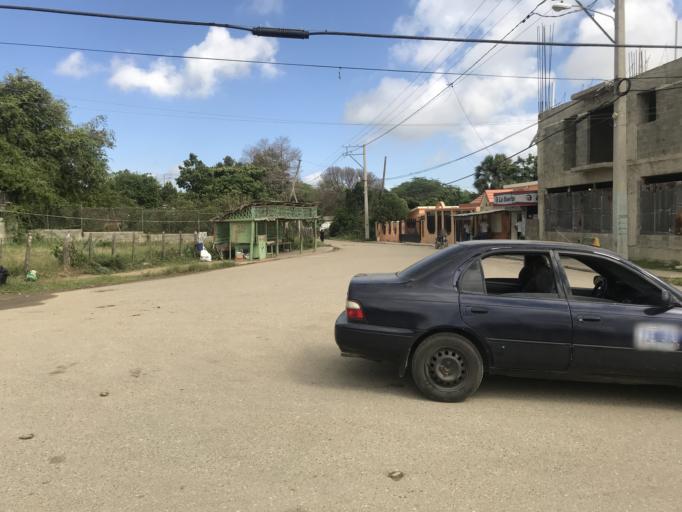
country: DO
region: Santiago
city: Santiago de los Caballeros
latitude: 19.3970
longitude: -70.6954
